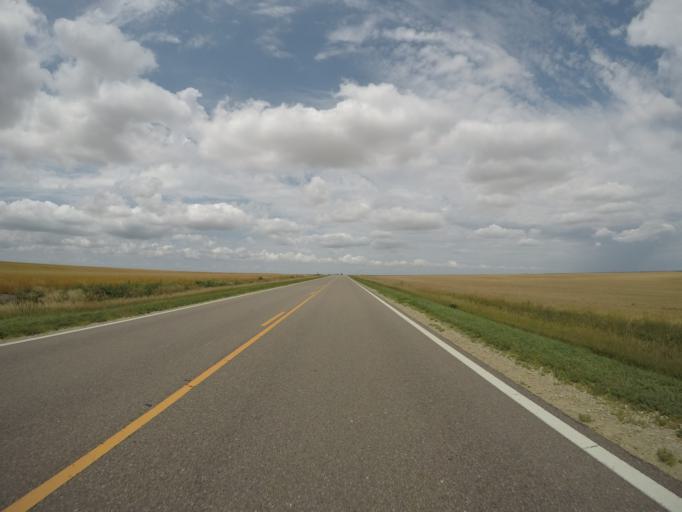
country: US
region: Kansas
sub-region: Rawlins County
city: Atwood
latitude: 39.6846
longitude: -101.0565
